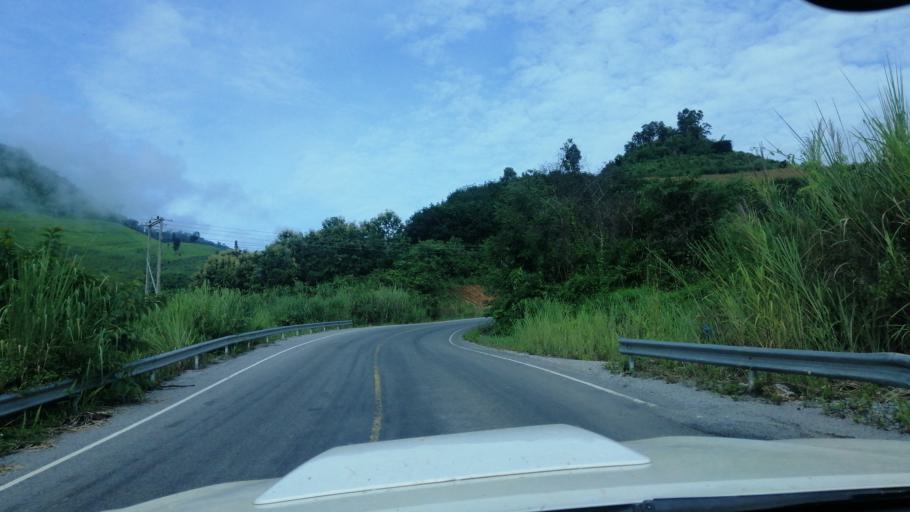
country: TH
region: Phayao
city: Phu Sang
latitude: 19.6740
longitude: 100.4753
